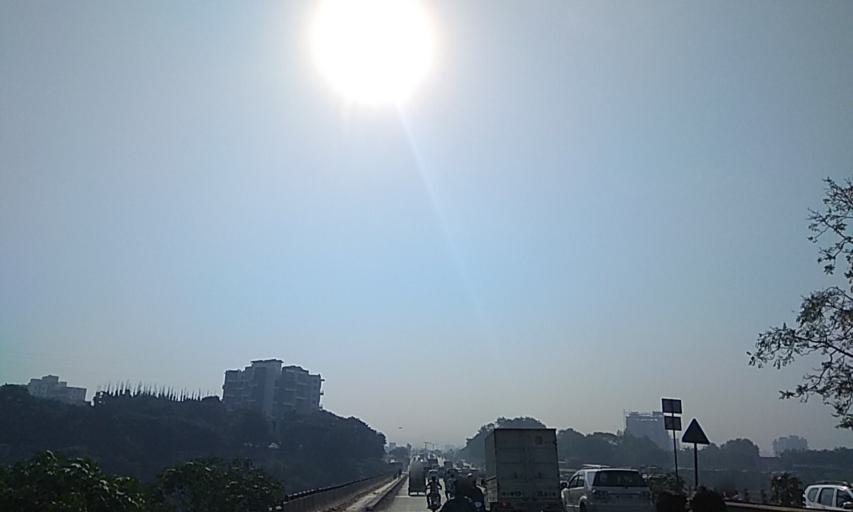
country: IN
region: Maharashtra
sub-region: Pune Division
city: Kharakvasla
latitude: 18.4754
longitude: 73.8088
